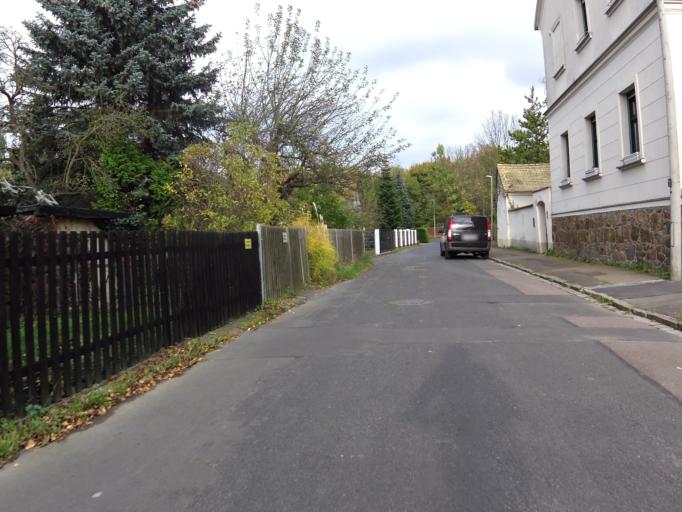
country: DE
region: Saxony
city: Taucha
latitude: 51.3814
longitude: 12.4392
